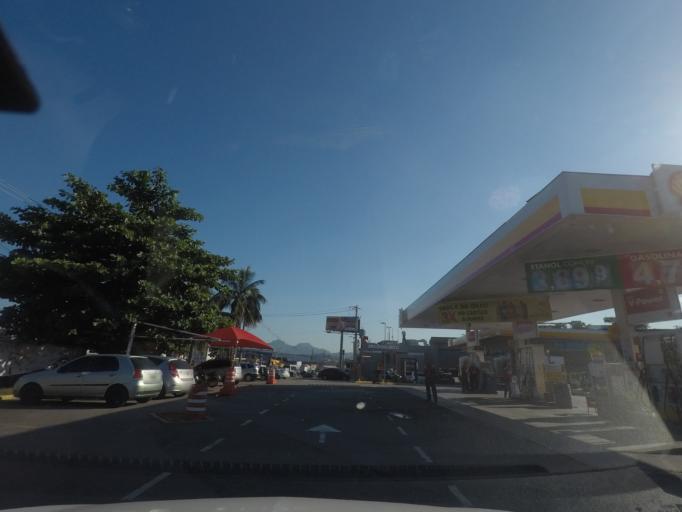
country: BR
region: Rio de Janeiro
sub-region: Duque De Caxias
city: Duque de Caxias
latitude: -22.7888
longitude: -43.2859
